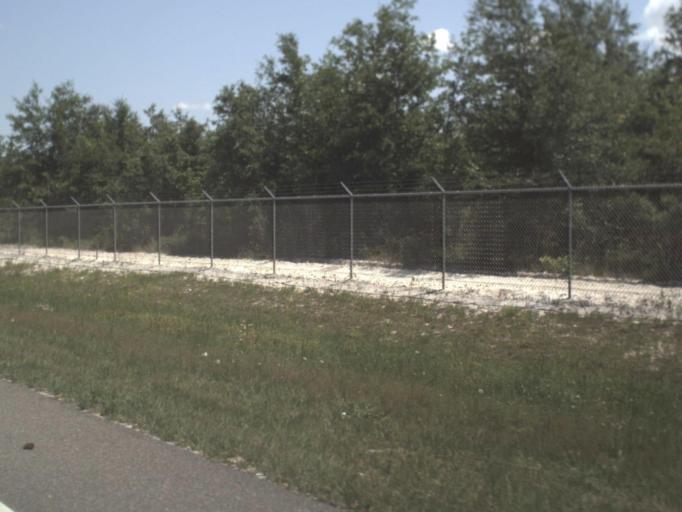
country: US
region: Florida
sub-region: Clay County
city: Keystone Heights
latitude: 29.8330
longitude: -82.0626
